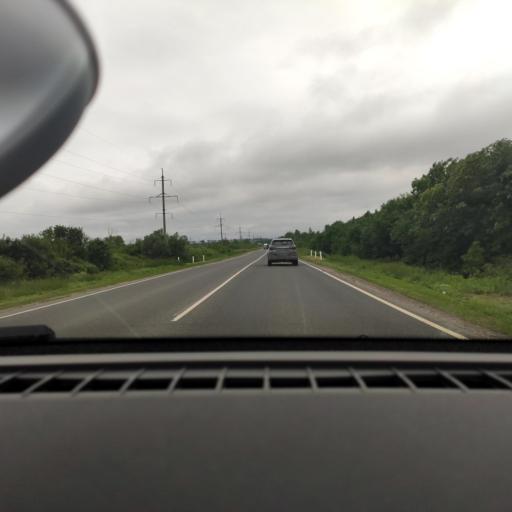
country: RU
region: Samara
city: Dubovyy Umet
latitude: 53.0928
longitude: 50.2857
